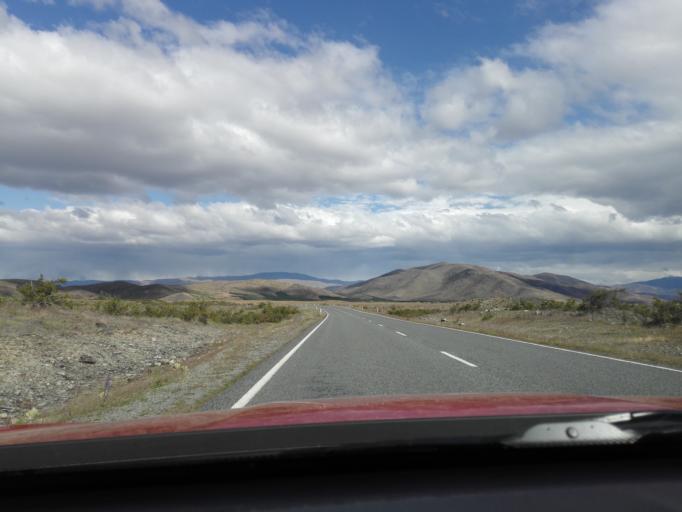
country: NZ
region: Canterbury
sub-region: Timaru District
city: Pleasant Point
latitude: -44.2005
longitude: 170.2509
